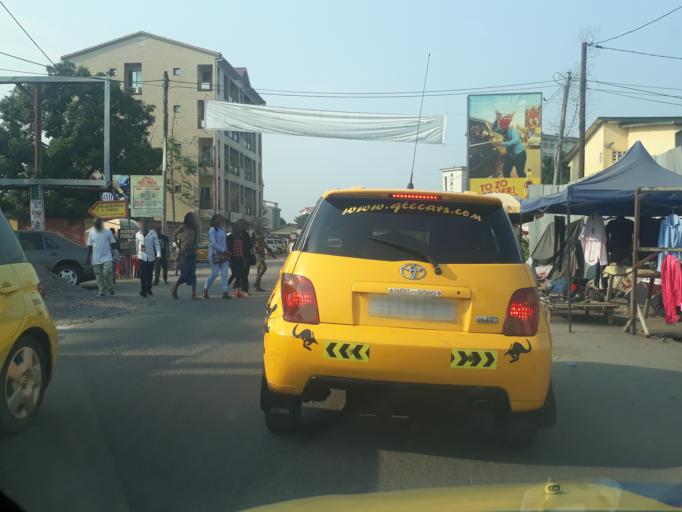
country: CD
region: Kinshasa
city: Kinshasa
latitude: -4.3189
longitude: 15.3299
